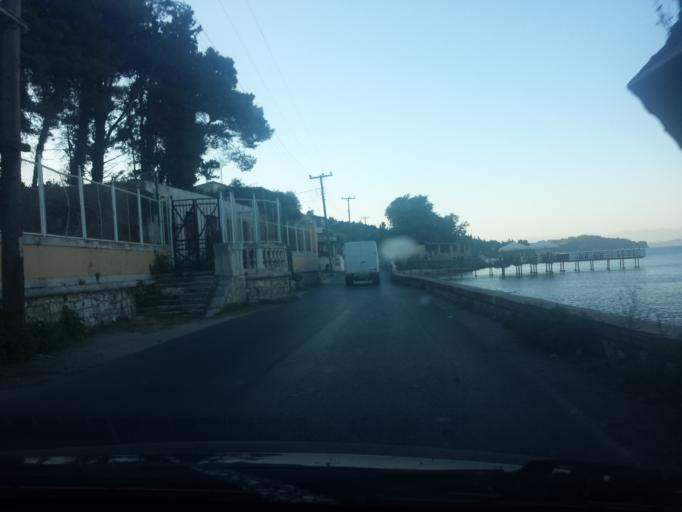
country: GR
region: Ionian Islands
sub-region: Nomos Kerkyras
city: Perama
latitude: 39.5634
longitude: 19.9102
